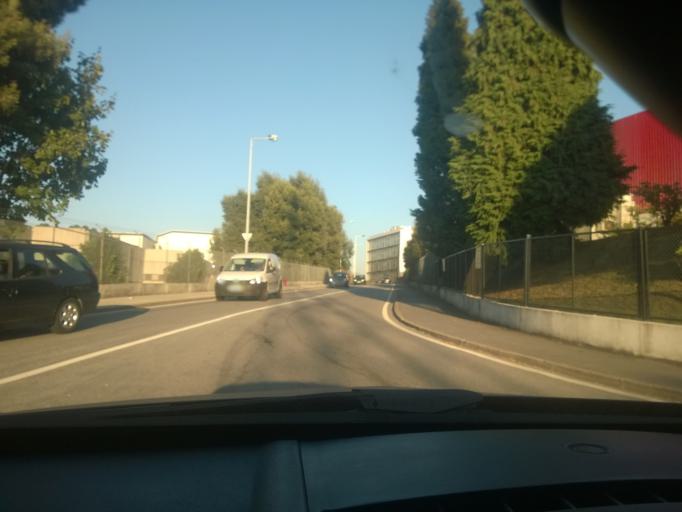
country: PT
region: Porto
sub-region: Maia
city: Gemunde
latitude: 41.2602
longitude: -8.6462
